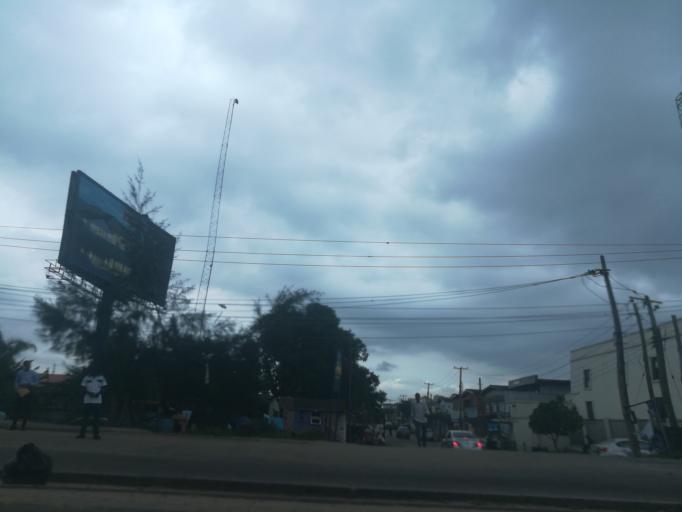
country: NG
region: Lagos
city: Somolu
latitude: 6.5488
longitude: 3.3789
